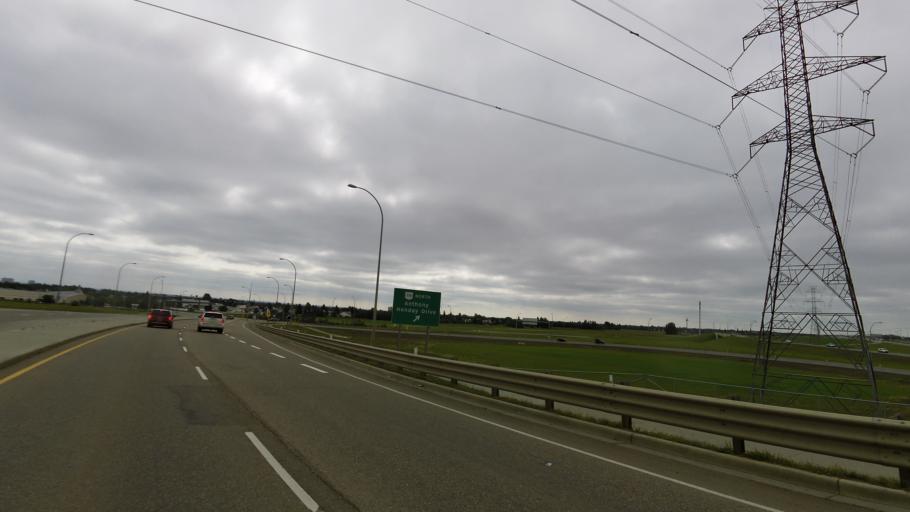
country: CA
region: Alberta
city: St. Albert
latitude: 53.5225
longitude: -113.6581
